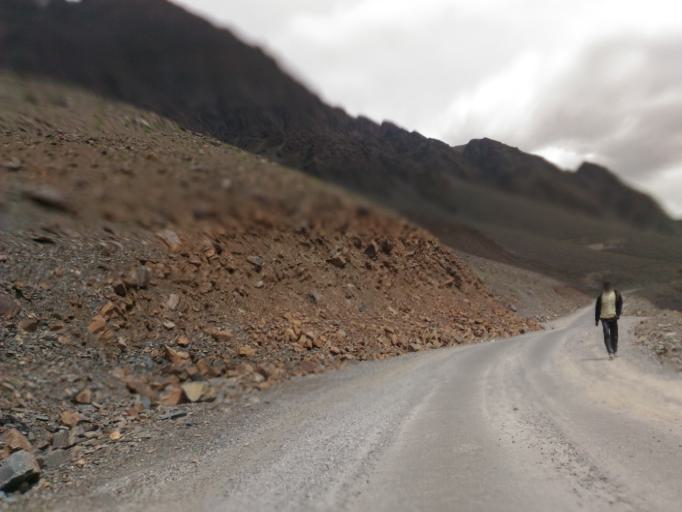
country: IN
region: Himachal Pradesh
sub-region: Lahul and Spiti
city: Kyelang
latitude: 32.7787
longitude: 77.3690
